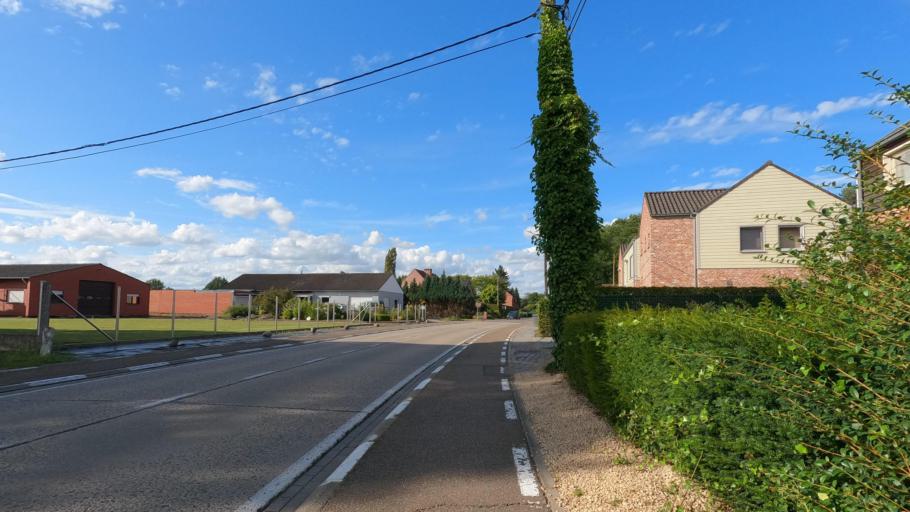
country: BE
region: Flanders
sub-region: Provincie Antwerpen
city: Herselt
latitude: 51.0342
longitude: 4.8888
